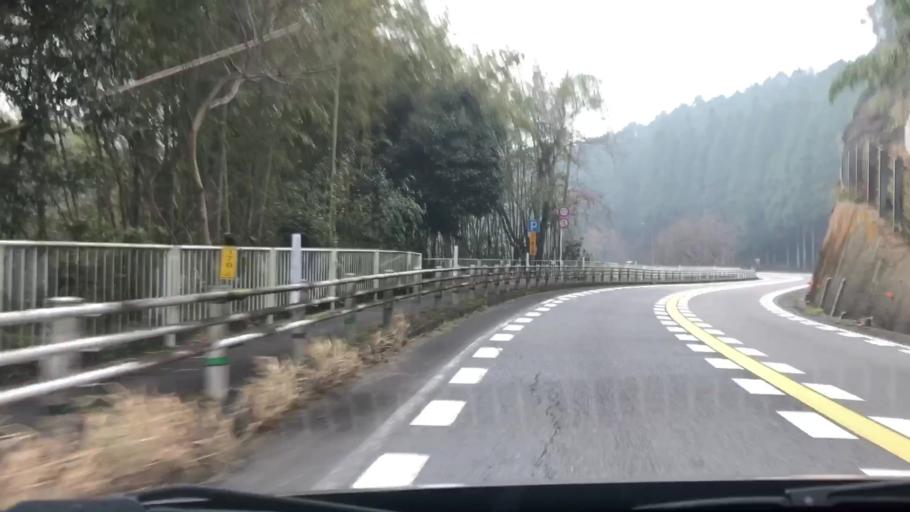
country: JP
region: Oita
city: Usuki
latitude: 33.0240
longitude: 131.6944
